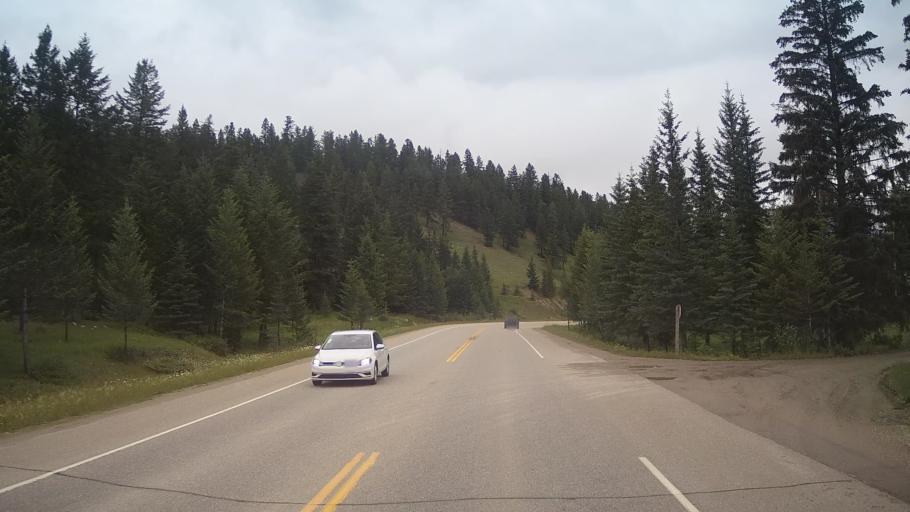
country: CA
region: Alberta
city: Jasper Park Lodge
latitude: 52.8922
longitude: -118.0759
